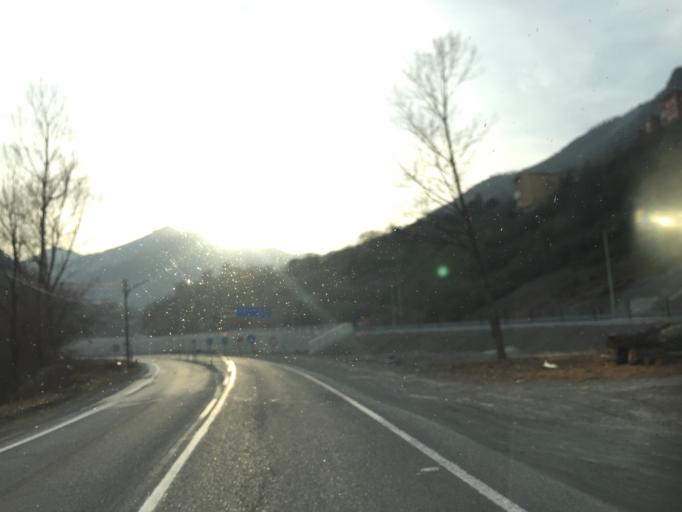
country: TR
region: Trabzon
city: Macka
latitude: 40.8082
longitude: 39.6000
